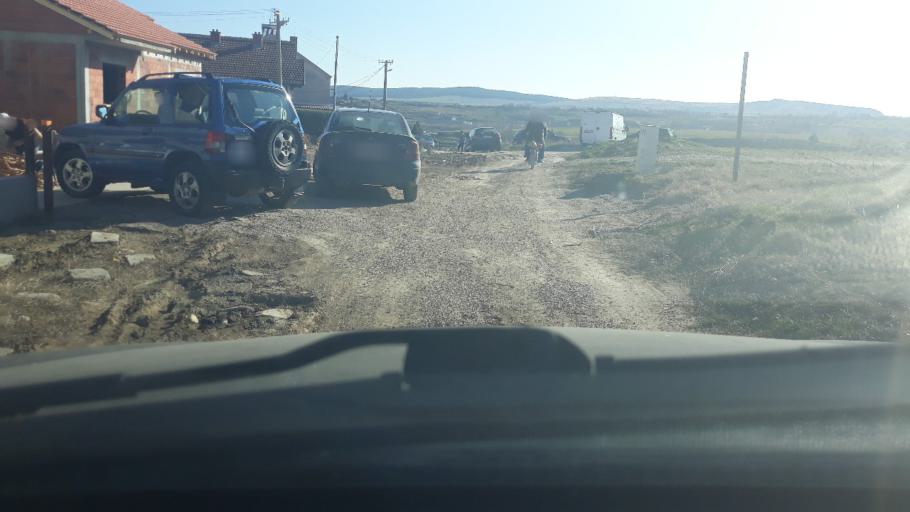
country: MK
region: Sveti Nikole
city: Sveti Nikole
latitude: 41.8689
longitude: 21.9301
